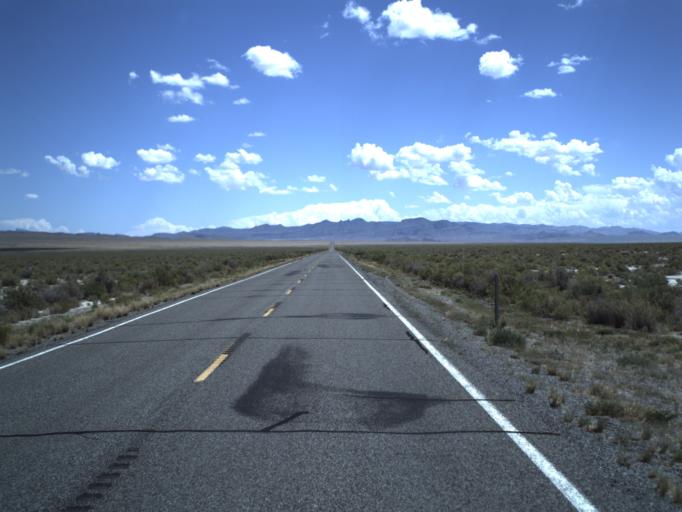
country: US
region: Nevada
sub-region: White Pine County
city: McGill
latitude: 39.0474
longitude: -113.9219
